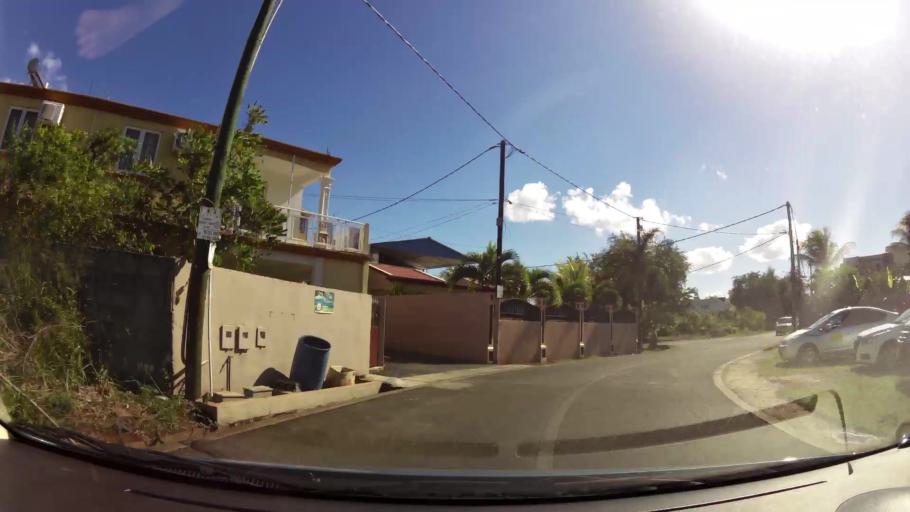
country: MU
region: Black River
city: Flic en Flac
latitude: -20.2852
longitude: 57.3692
